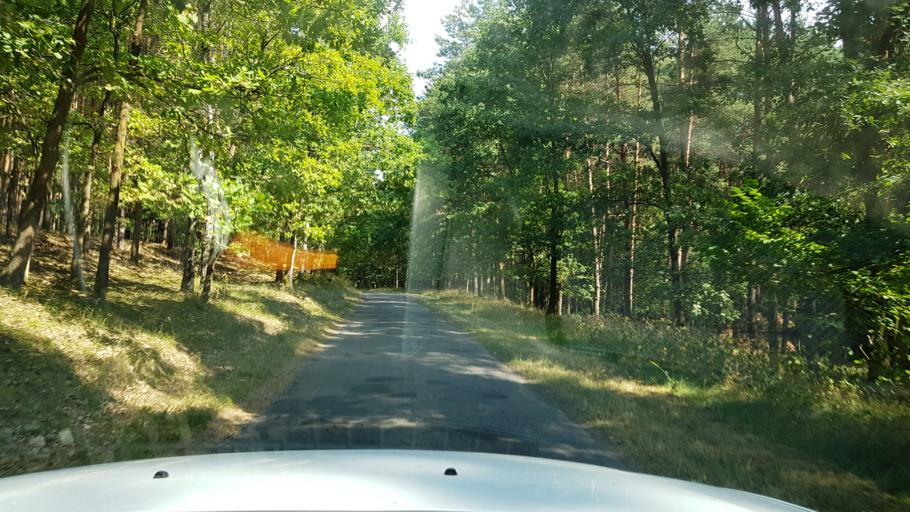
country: PL
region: West Pomeranian Voivodeship
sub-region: Powiat gryfinski
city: Moryn
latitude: 52.8129
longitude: 14.3250
